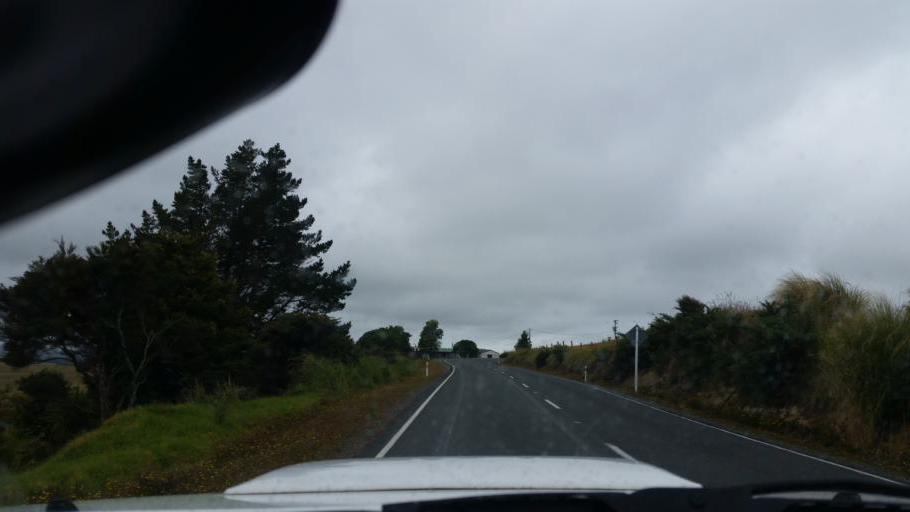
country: NZ
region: Auckland
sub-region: Auckland
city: Wellsford
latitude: -36.1321
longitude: 174.5299
